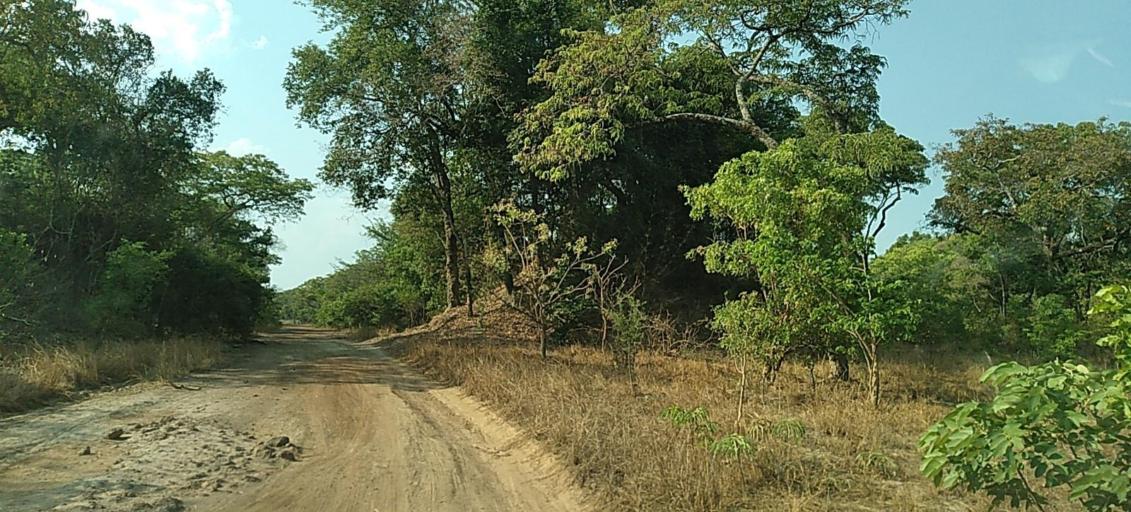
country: ZM
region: Copperbelt
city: Mpongwe
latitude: -13.4436
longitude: 28.0623
